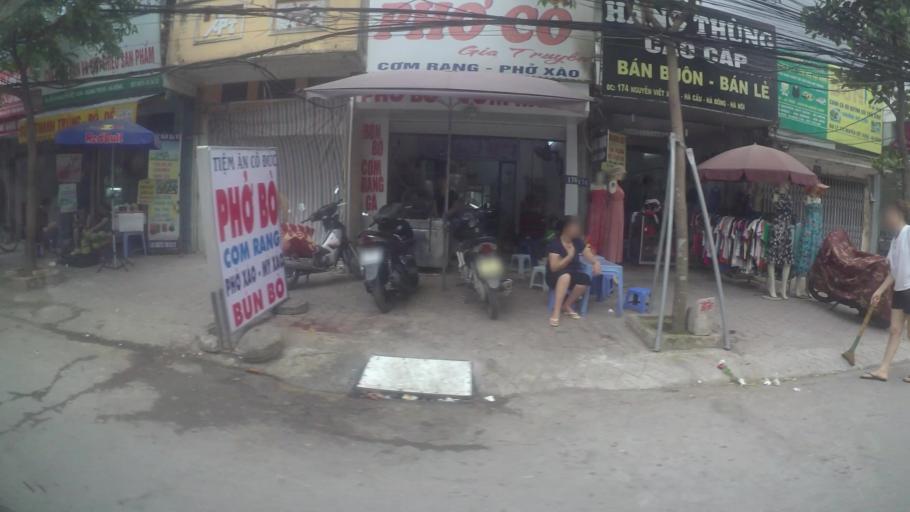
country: VN
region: Ha Noi
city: Ha Dong
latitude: 20.9696
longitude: 105.7679
